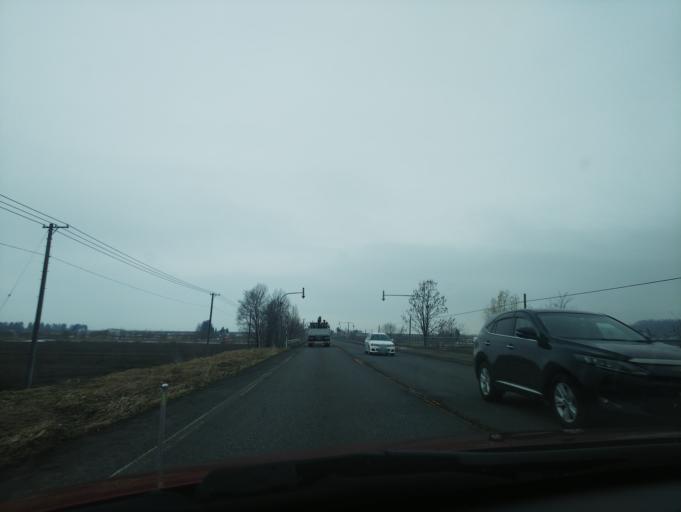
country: JP
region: Hokkaido
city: Nayoro
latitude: 44.0657
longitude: 142.3983
